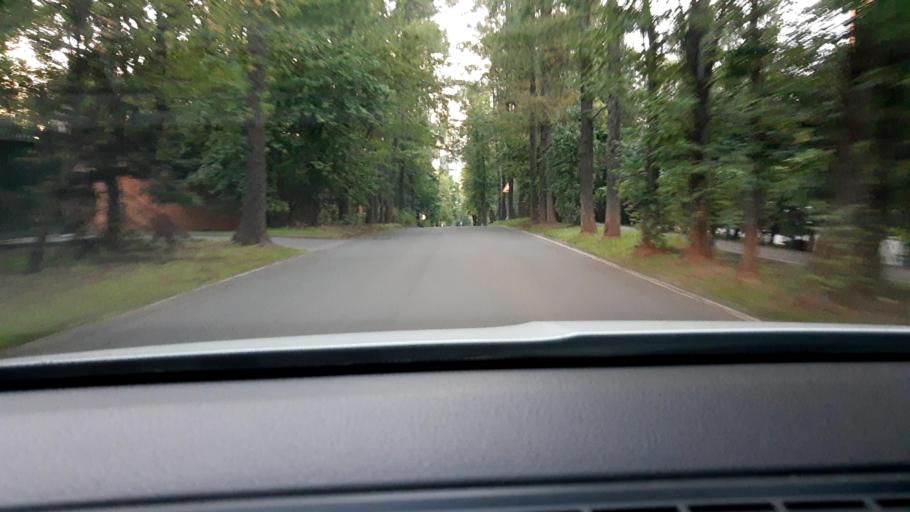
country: RU
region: Moskovskaya
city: Zarech'ye
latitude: 55.6870
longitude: 37.3834
